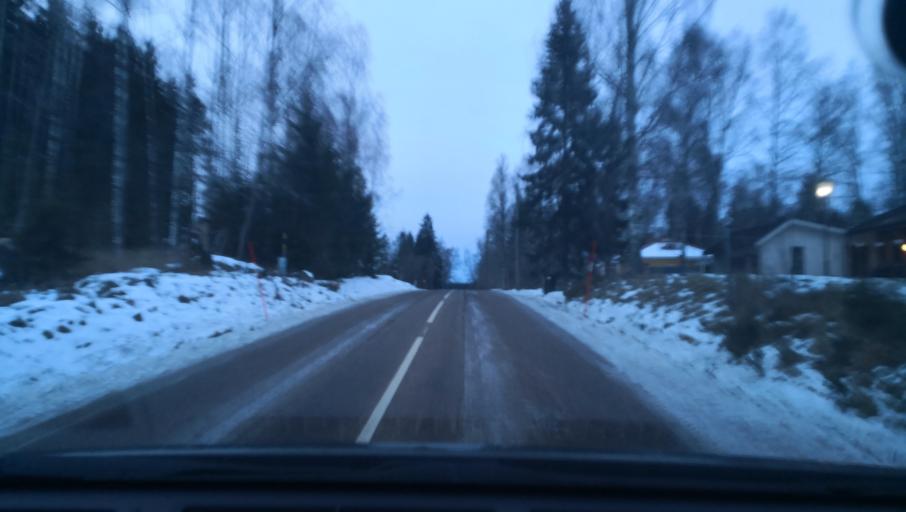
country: SE
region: Dalarna
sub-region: Avesta Kommun
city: Horndal
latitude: 60.1942
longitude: 16.4655
